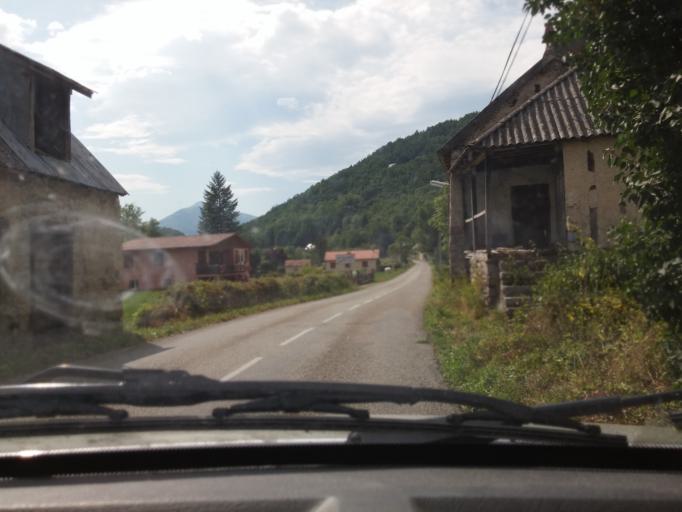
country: FR
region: Midi-Pyrenees
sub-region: Departement de l'Ariege
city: Saint-Girons
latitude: 42.8601
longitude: 1.2631
